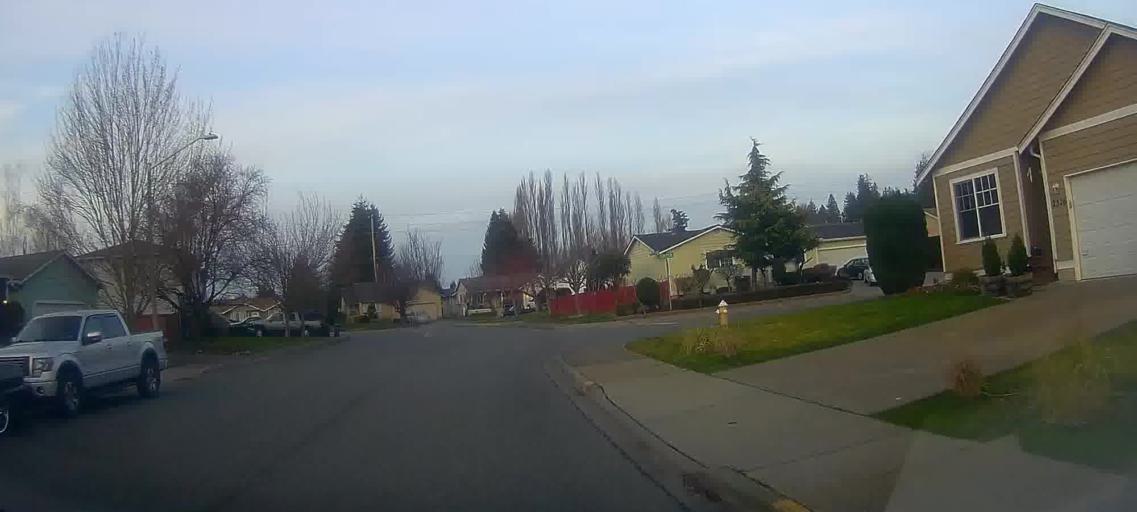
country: US
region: Washington
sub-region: Skagit County
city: Mount Vernon
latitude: 48.4418
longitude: -122.3272
